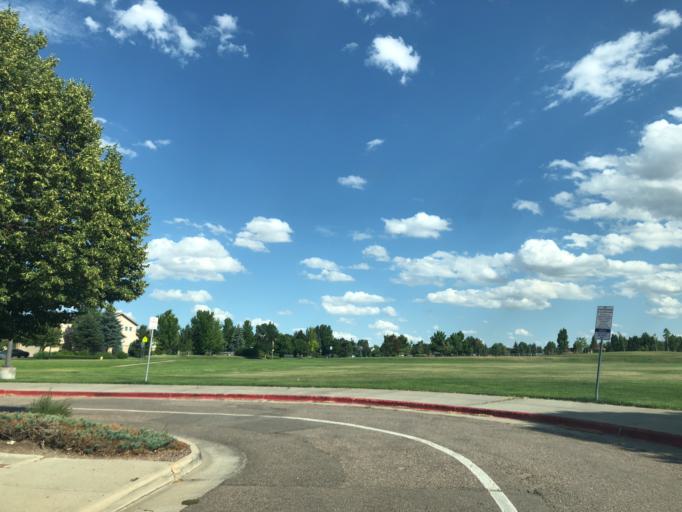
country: US
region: Colorado
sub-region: Arapahoe County
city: Dove Valley
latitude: 39.6012
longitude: -104.7817
